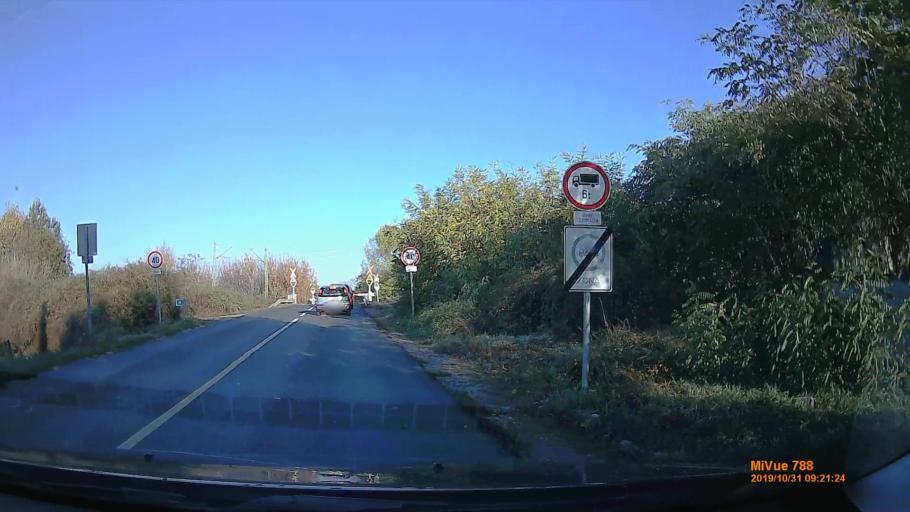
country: HU
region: Pest
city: Maglod
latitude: 47.4306
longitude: 19.3807
